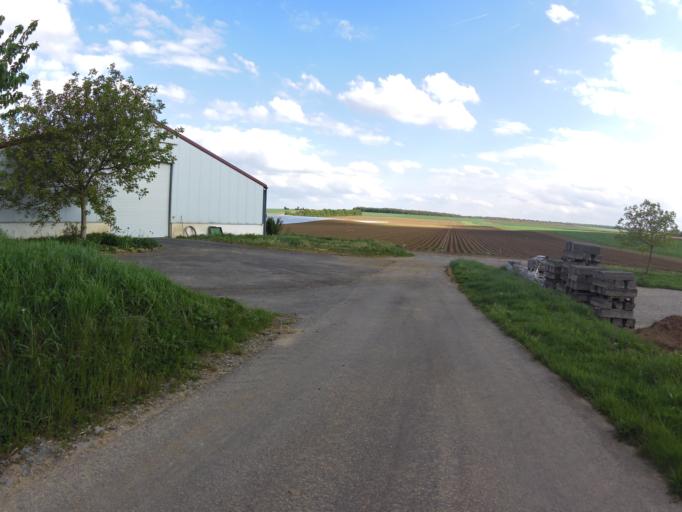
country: DE
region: Bavaria
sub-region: Regierungsbezirk Unterfranken
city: Unterpleichfeld
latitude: 49.8627
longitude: 10.0625
